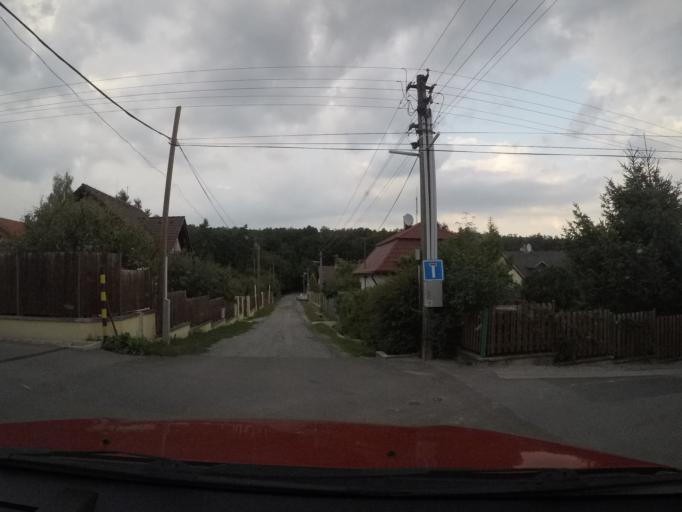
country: SK
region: Kosicky
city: Kosice
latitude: 48.6934
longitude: 21.2105
